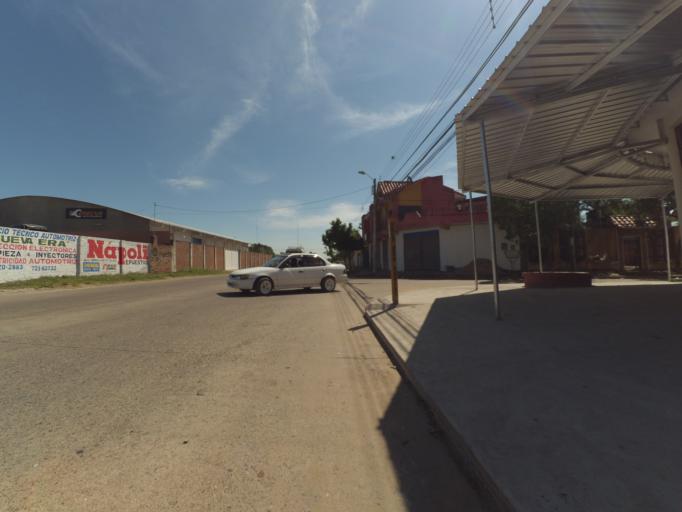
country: BO
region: Santa Cruz
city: Santa Cruz de la Sierra
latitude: -17.8104
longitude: -63.2031
